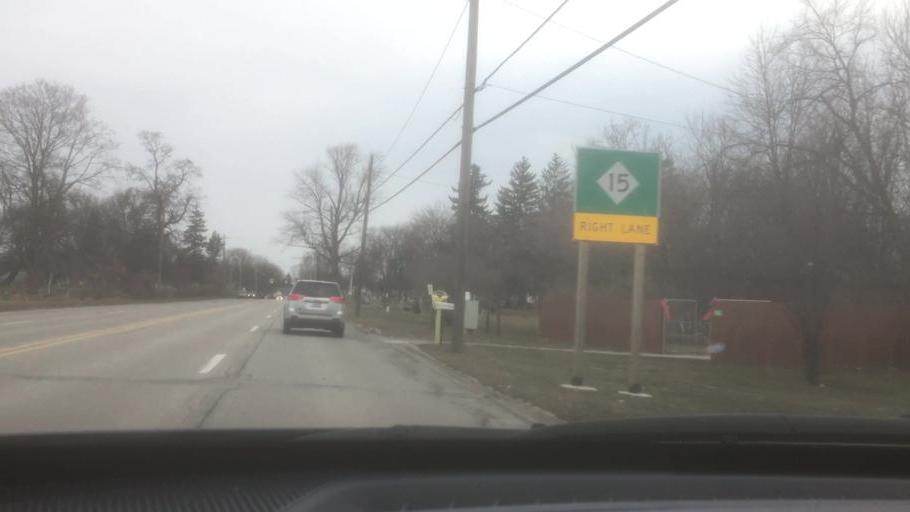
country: US
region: Michigan
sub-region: Bay County
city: Bay City
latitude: 43.5875
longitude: -83.8634
